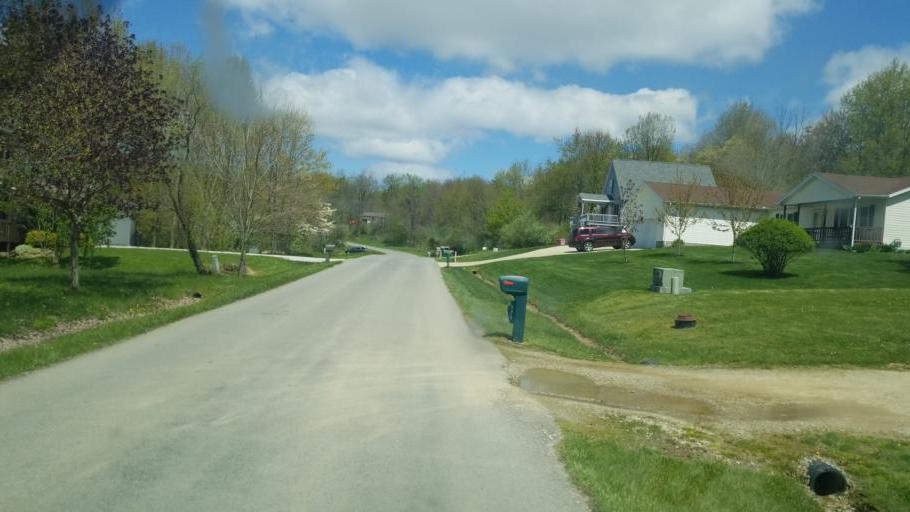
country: US
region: Ohio
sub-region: Knox County
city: Gambier
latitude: 40.4418
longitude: -82.3642
